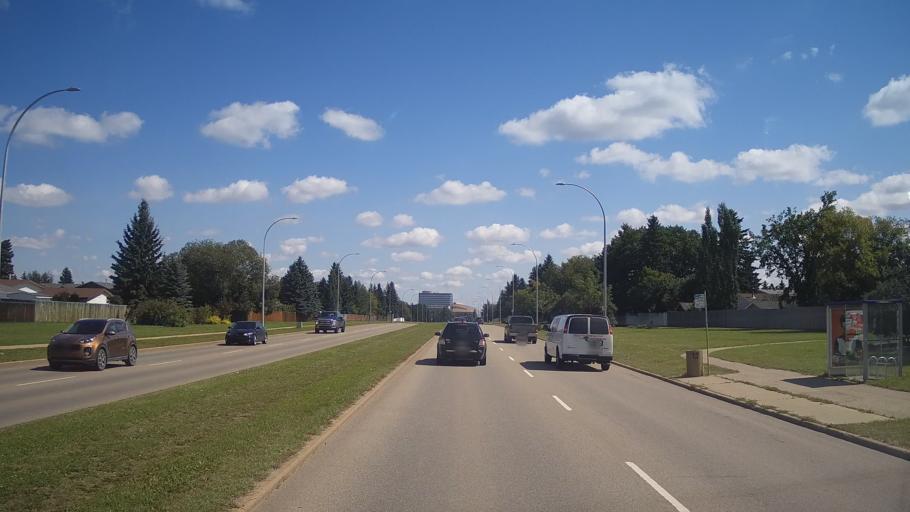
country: CA
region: Alberta
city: St. Albert
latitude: 53.5214
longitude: -113.6471
